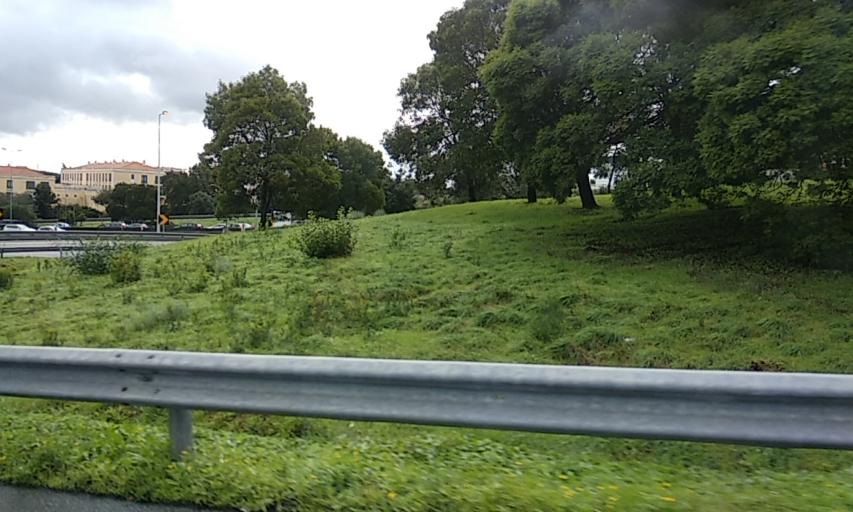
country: PT
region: Lisbon
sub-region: Oeiras
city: Barcarena
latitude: 38.7487
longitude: -9.2719
